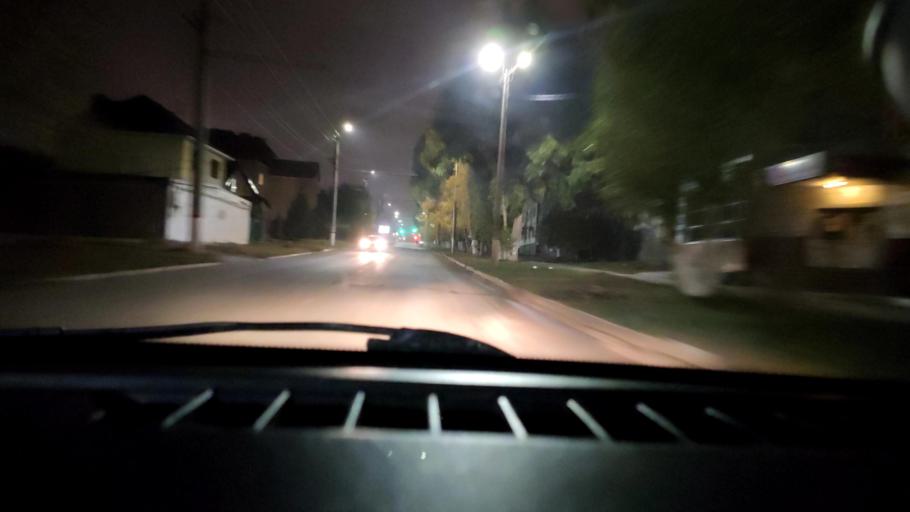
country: RU
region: Samara
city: Novokuybyshevsk
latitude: 53.1064
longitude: 49.9569
